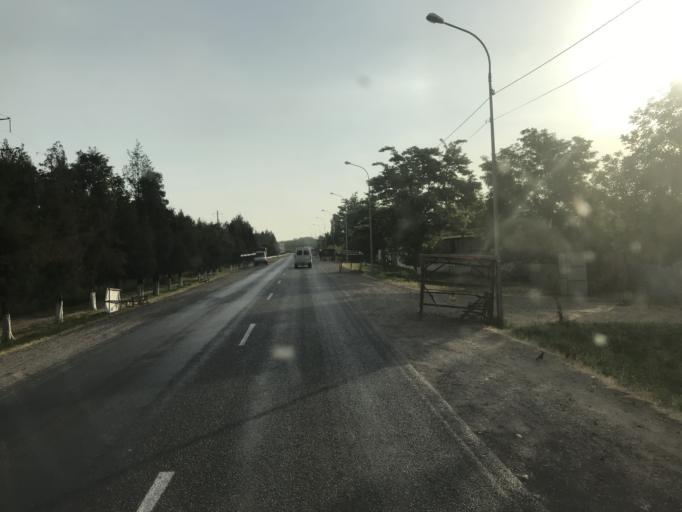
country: KZ
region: Ongtustik Qazaqstan
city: Saryaghash
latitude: 41.4868
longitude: 69.2568
